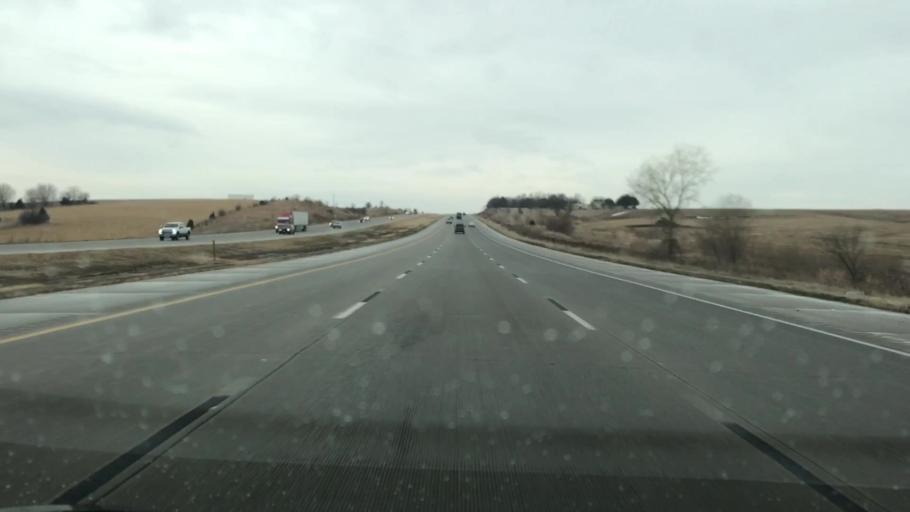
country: US
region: Nebraska
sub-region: Sarpy County
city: Chalco
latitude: 41.1319
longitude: -96.1800
